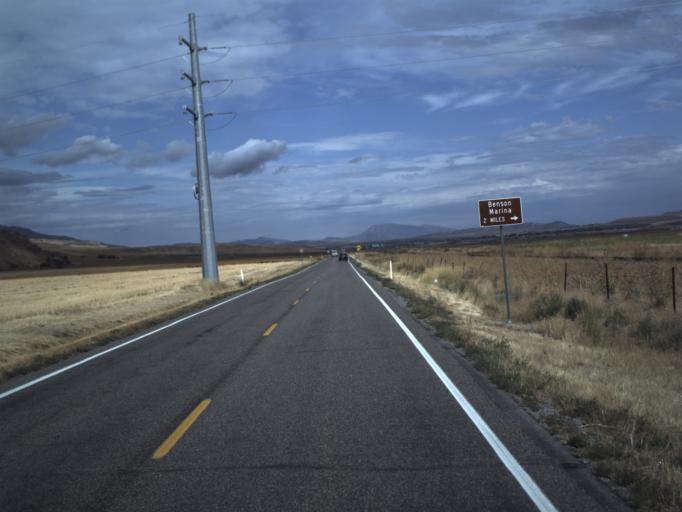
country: US
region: Utah
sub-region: Cache County
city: Benson
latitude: 41.7837
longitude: -111.9864
